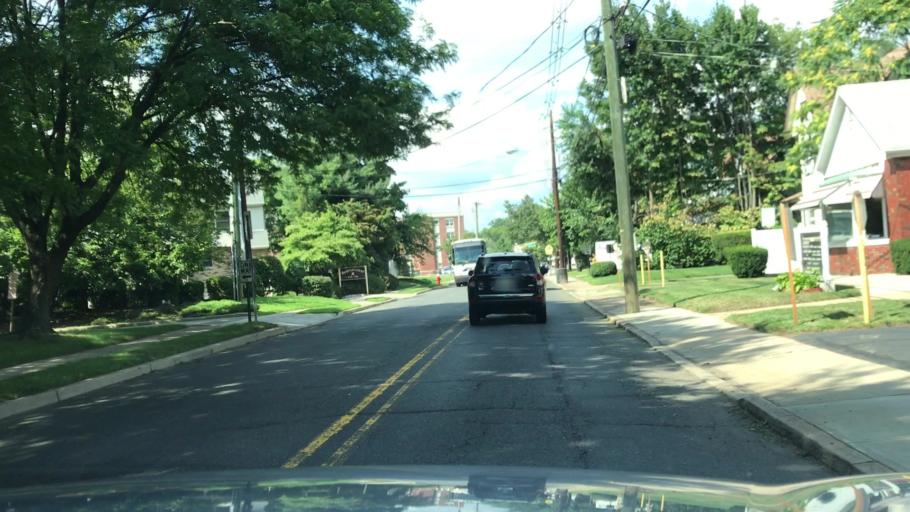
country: US
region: New Jersey
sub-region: Bergen County
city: Dumont
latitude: 40.9426
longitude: -73.9930
